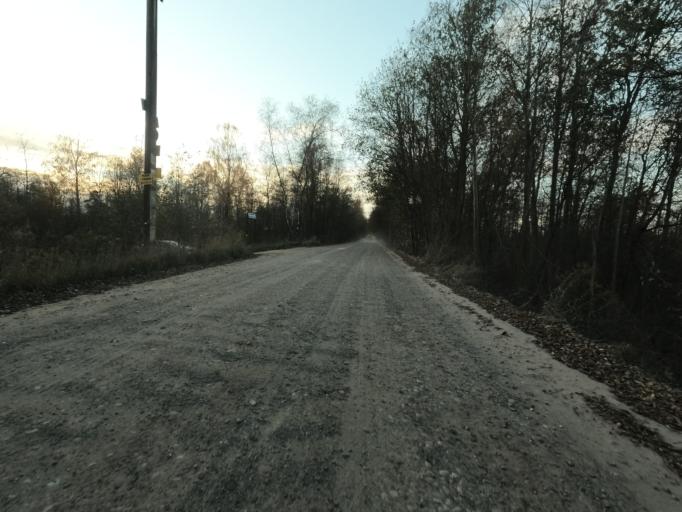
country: RU
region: Leningrad
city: Mga
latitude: 59.7684
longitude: 31.2353
